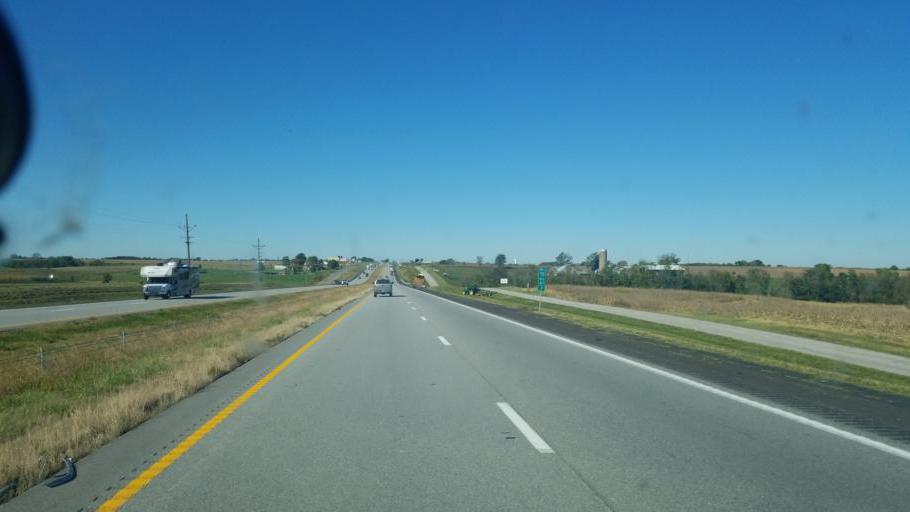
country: US
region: Missouri
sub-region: Lafayette County
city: Concordia
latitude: 38.9881
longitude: -93.5227
